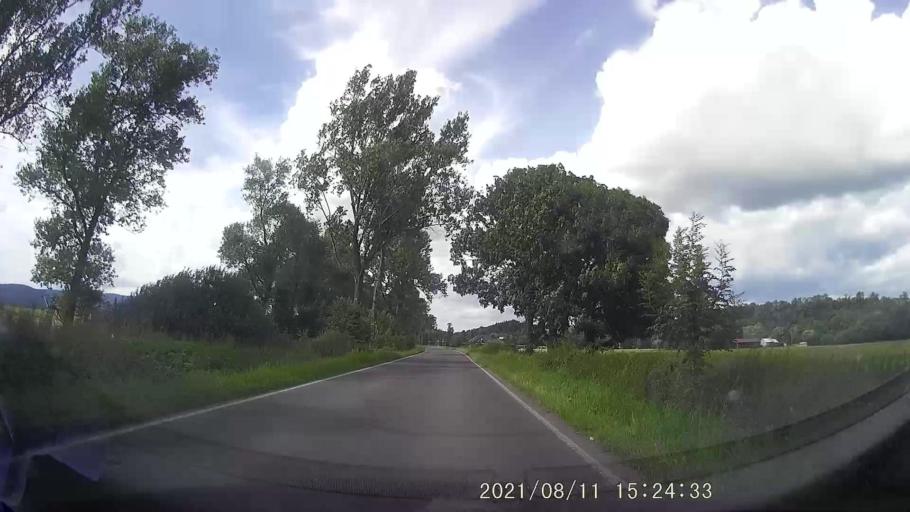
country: PL
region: Lower Silesian Voivodeship
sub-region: Powiat klodzki
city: Bystrzyca Klodzka
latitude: 50.2803
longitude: 16.6832
